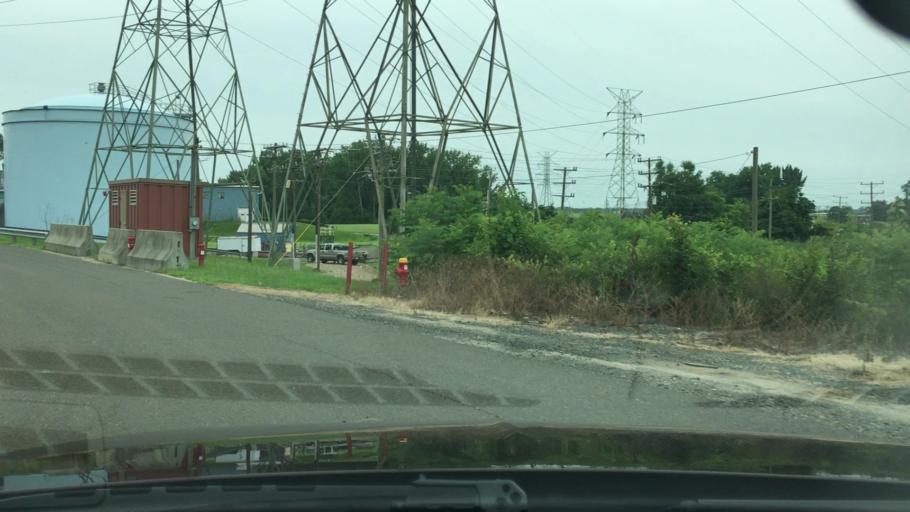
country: US
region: Connecticut
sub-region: Hartford County
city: Hartford
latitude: 41.7497
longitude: -72.6540
